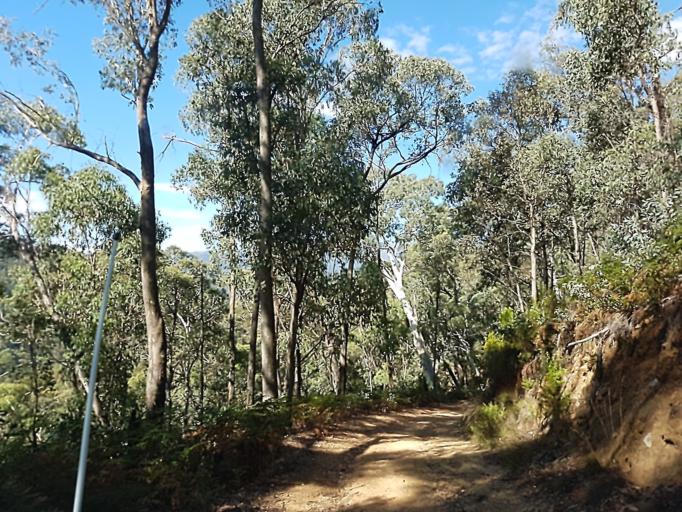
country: AU
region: Victoria
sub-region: Alpine
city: Mount Beauty
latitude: -36.9276
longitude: 147.0153
